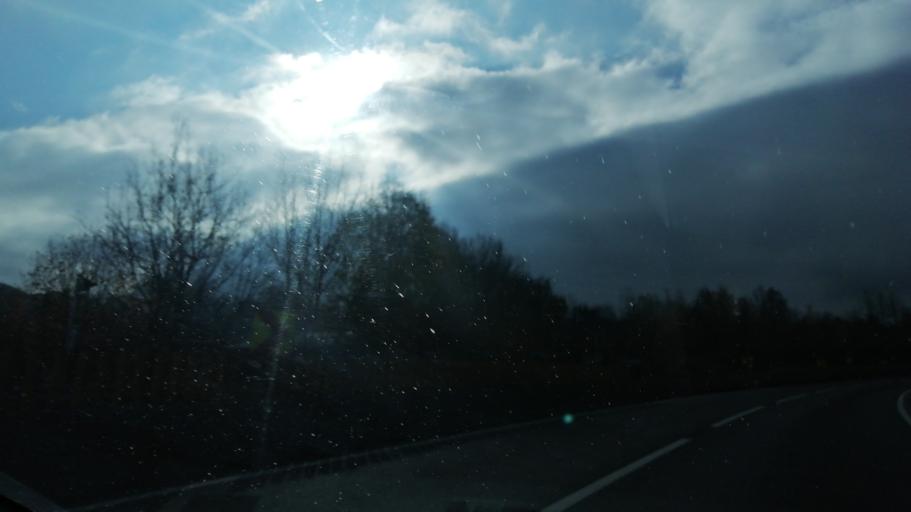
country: TR
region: Duzce
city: Kaynasli
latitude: 40.7665
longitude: 31.3568
